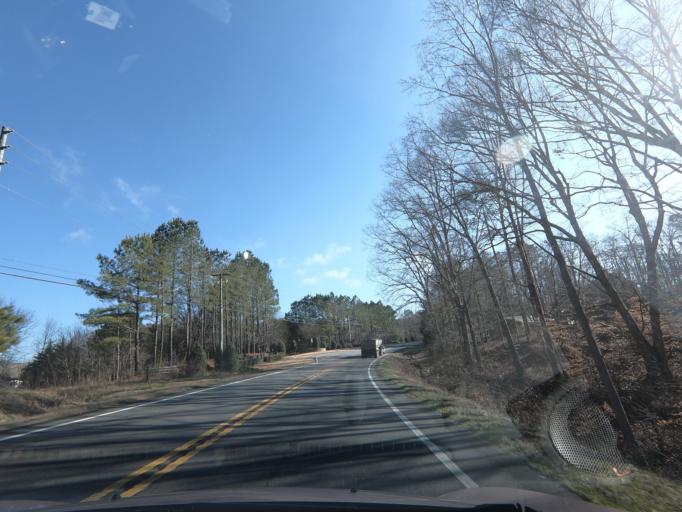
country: US
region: Georgia
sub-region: Cherokee County
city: Ball Ground
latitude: 34.2989
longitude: -84.2498
